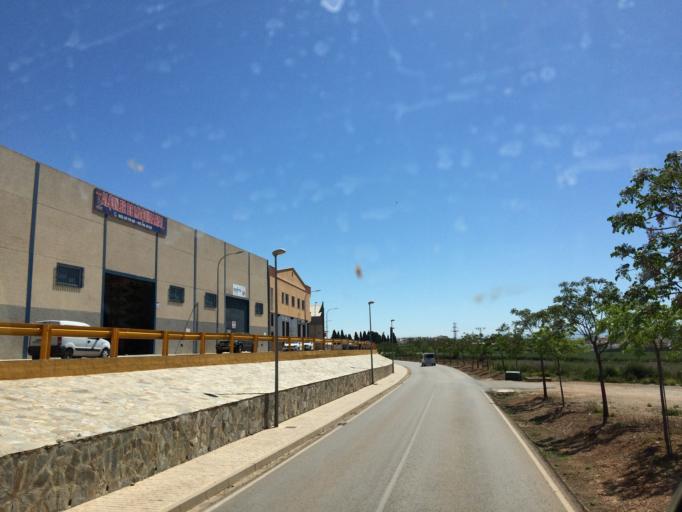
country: ES
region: Andalusia
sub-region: Provincia de Malaga
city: Campillos
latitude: 37.0489
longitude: -4.8748
